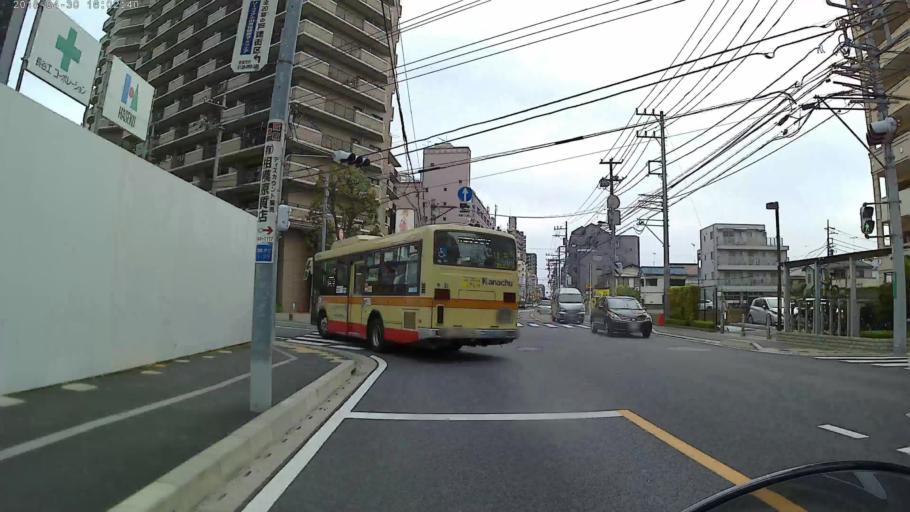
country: JP
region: Tokyo
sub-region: Machida-shi
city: Machida
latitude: 35.5146
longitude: 139.4212
